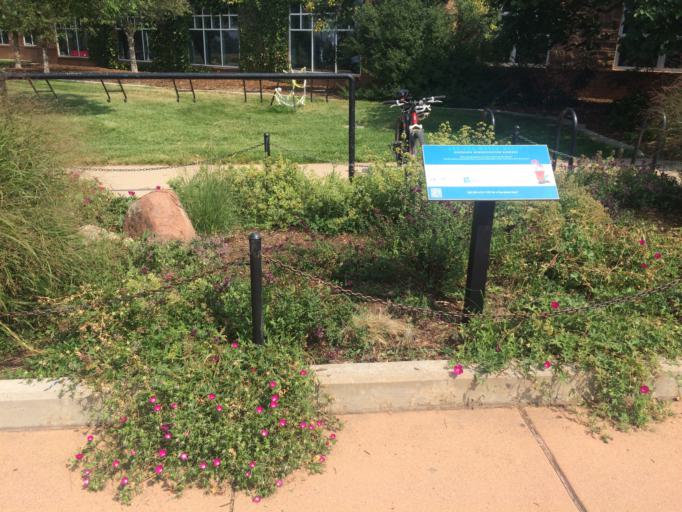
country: US
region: Colorado
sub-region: Boulder County
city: Boulder
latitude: 39.9923
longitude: -105.2201
